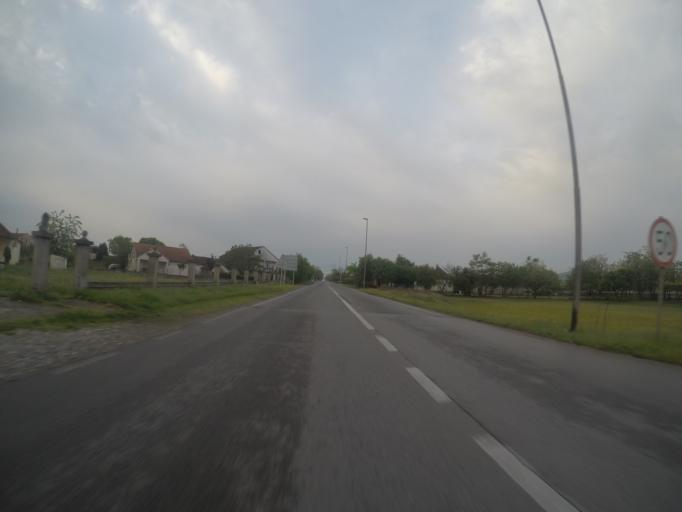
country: ME
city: Mojanovici
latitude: 42.3432
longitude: 19.2218
